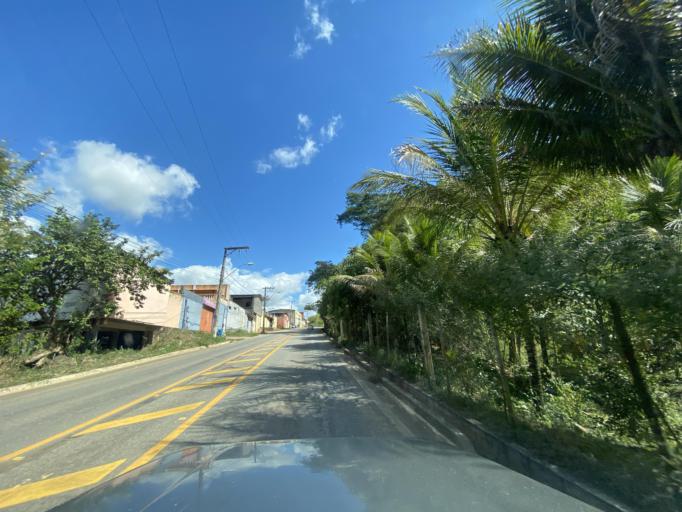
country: BR
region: Espirito Santo
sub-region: Alegre
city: Alegre
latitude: -20.7613
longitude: -41.5190
